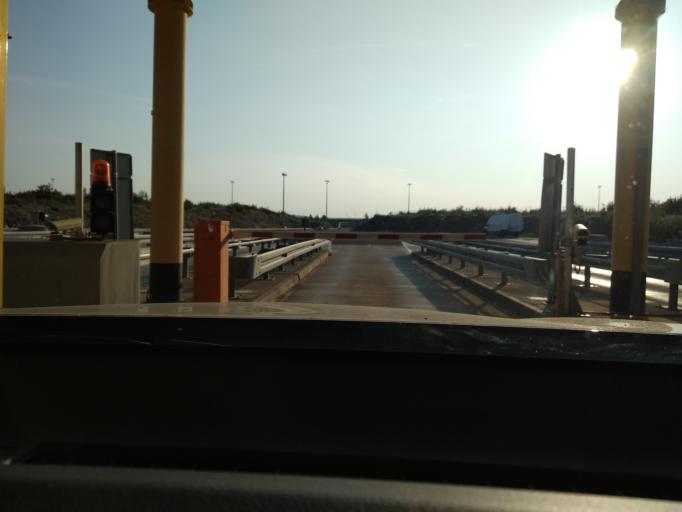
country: HR
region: Sibensko-Kniniska
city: Zaton
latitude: 43.8867
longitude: 15.7858
